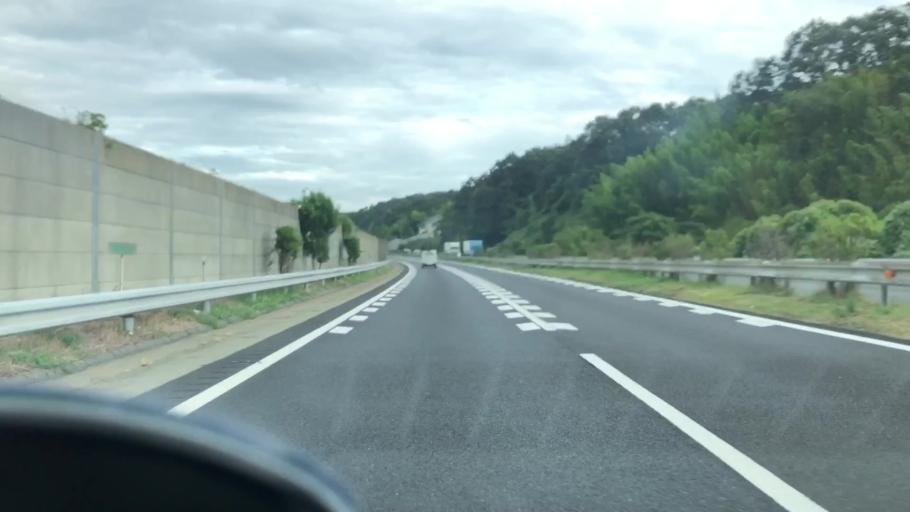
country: JP
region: Hyogo
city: Yashiro
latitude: 34.9008
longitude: 135.0696
